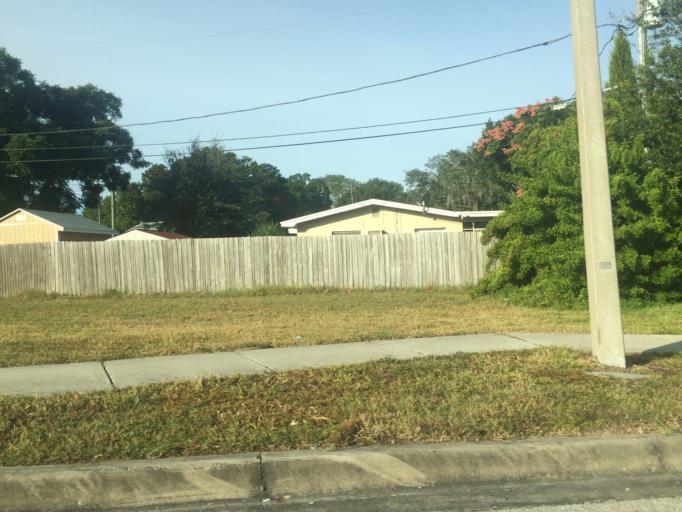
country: US
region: Florida
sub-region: Pinellas County
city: Clearwater
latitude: 27.9598
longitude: -82.7628
